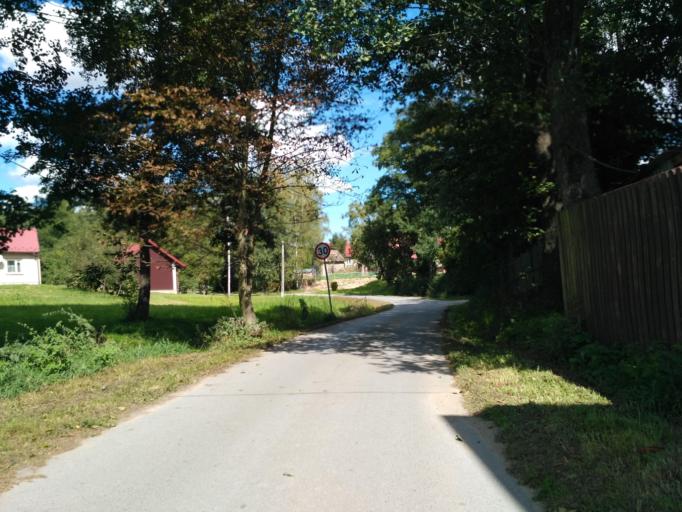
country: PL
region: Subcarpathian Voivodeship
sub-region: Powiat jasielski
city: Jaslo
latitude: 49.7589
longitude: 21.5023
